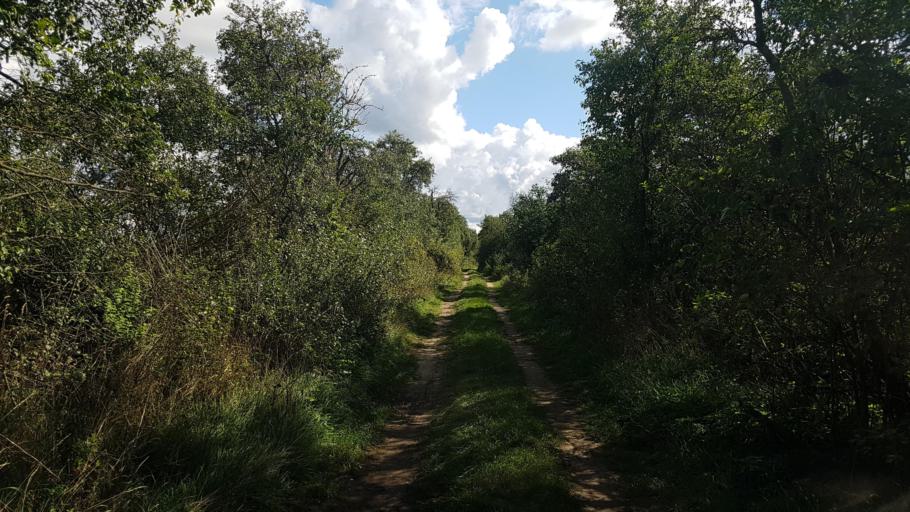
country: DE
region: Brandenburg
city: Niemegk
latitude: 52.0716
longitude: 12.7553
